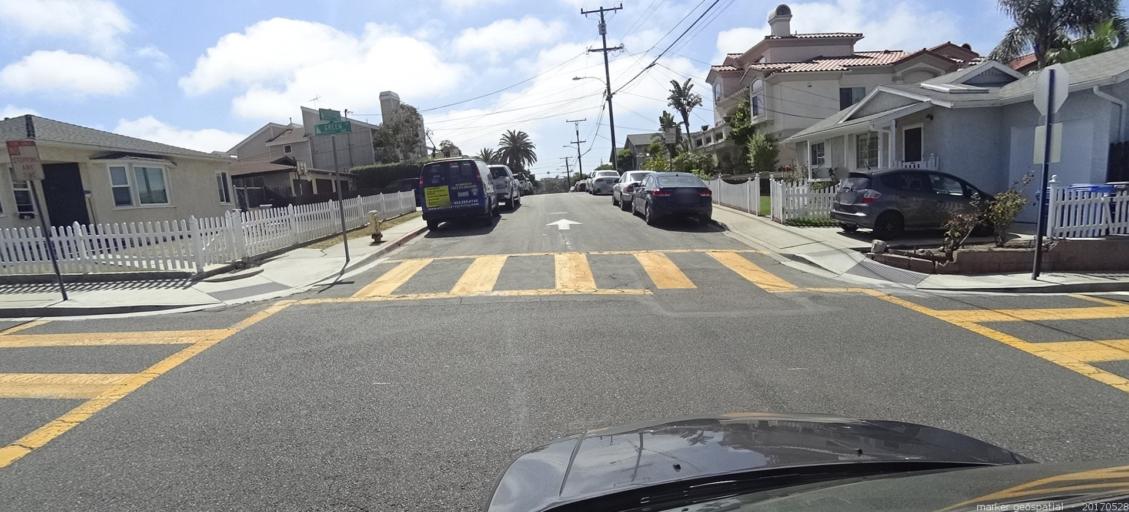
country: US
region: California
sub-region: Los Angeles County
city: Redondo Beach
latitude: 33.8700
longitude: -118.3769
